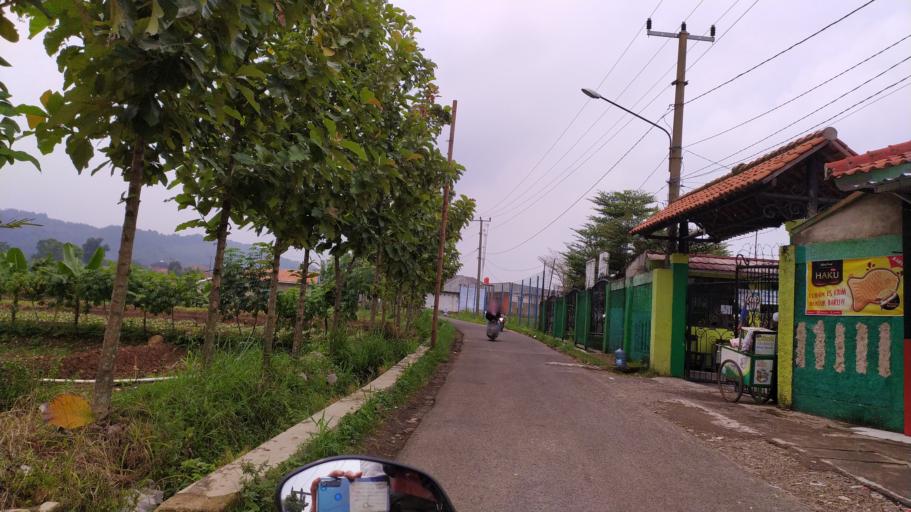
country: ID
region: West Java
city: Ciampea
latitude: -6.6129
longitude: 106.7096
